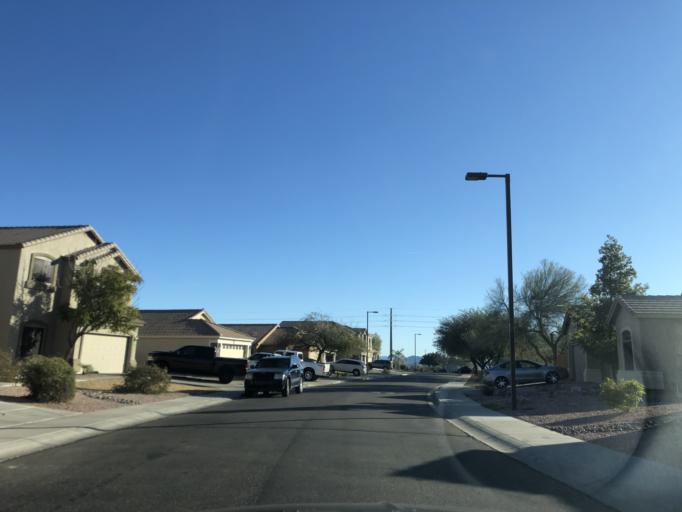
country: US
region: Arizona
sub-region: Maricopa County
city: Buckeye
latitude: 33.4373
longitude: -112.5677
